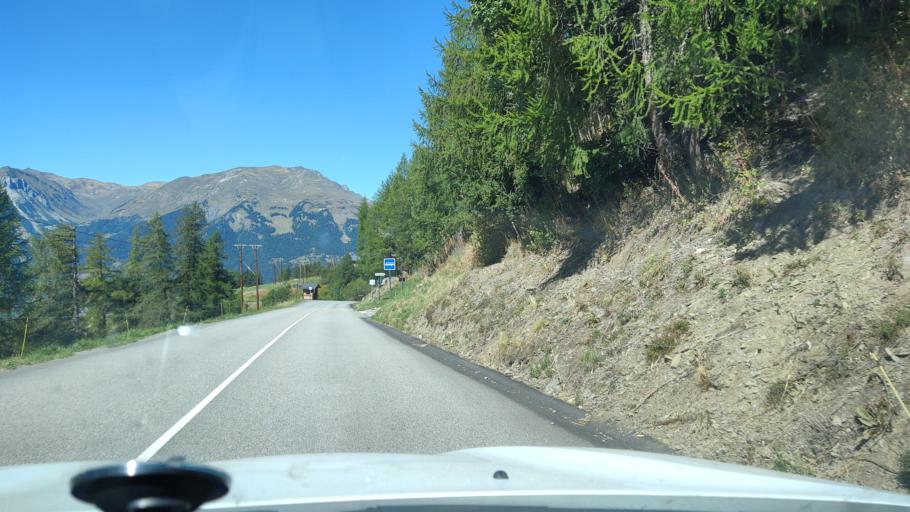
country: FR
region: Rhone-Alpes
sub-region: Departement de la Savoie
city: Macot-la-Plagne
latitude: 45.5257
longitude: 6.6770
